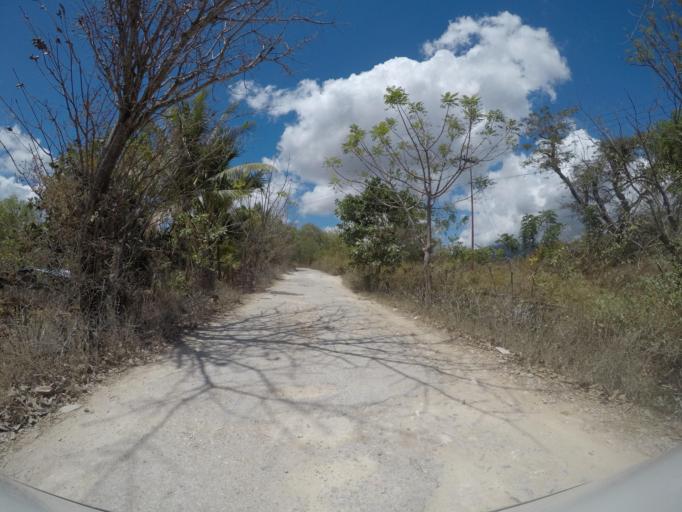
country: TL
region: Baucau
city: Baucau
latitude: -8.4834
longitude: 126.6272
